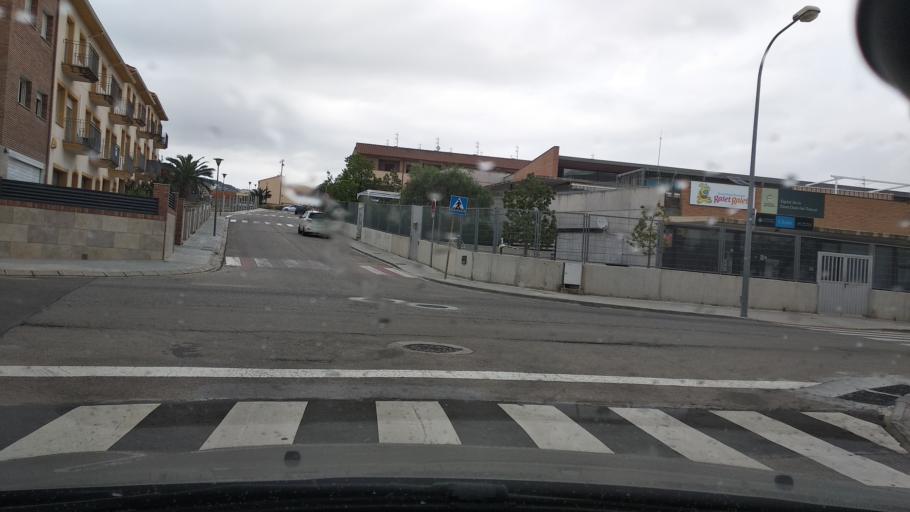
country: ES
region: Catalonia
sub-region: Provincia de Tarragona
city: El Vendrell
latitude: 41.2161
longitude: 1.5268
